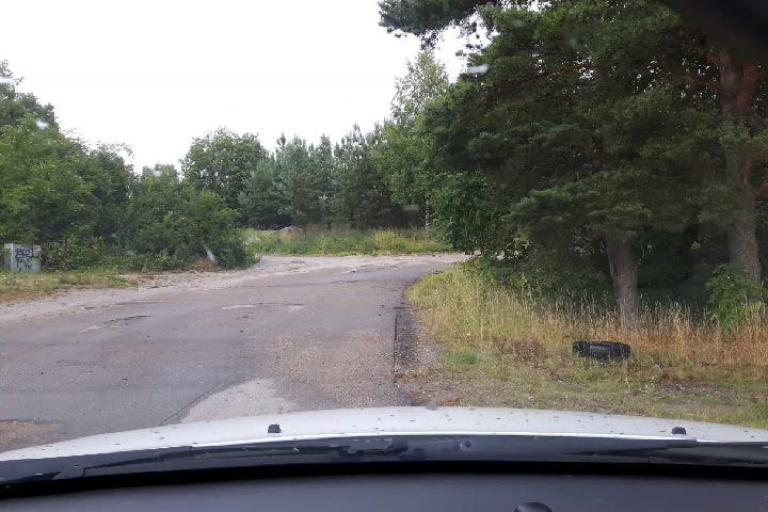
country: SE
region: Uppsala
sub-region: Uppsala Kommun
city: Gamla Uppsala
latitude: 59.8835
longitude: 17.6204
